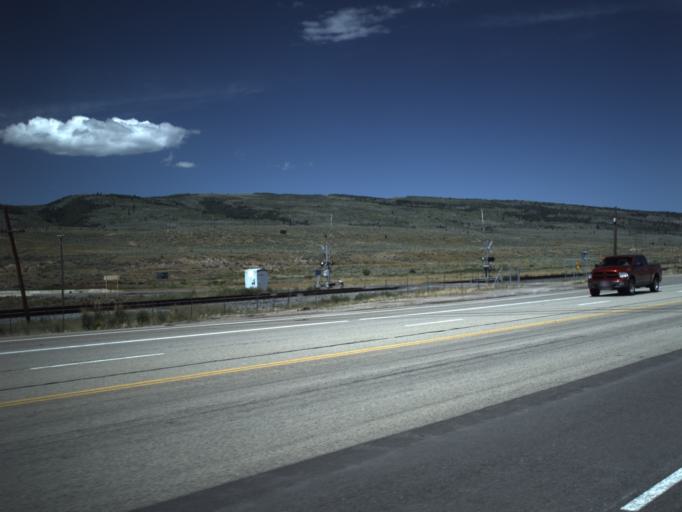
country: US
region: Utah
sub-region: Carbon County
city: Helper
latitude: 39.8614
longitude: -111.0261
